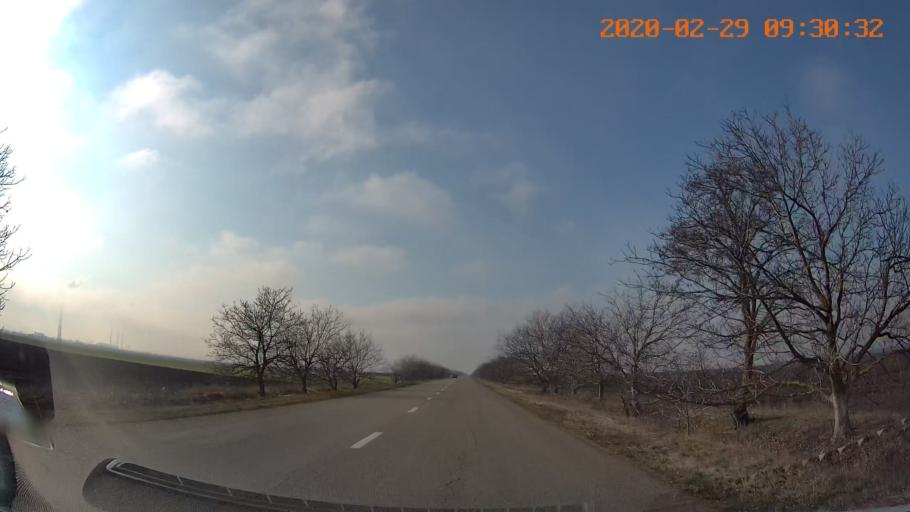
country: MD
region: Telenesti
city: Dnestrovsc
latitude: 46.6652
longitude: 29.9161
